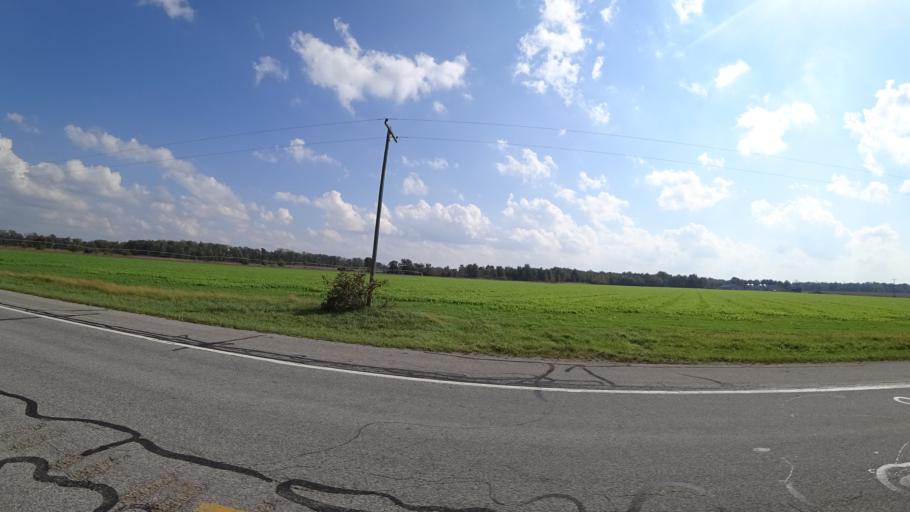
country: US
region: Michigan
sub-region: Saint Joseph County
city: Colon
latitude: 42.0410
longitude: -85.3159
